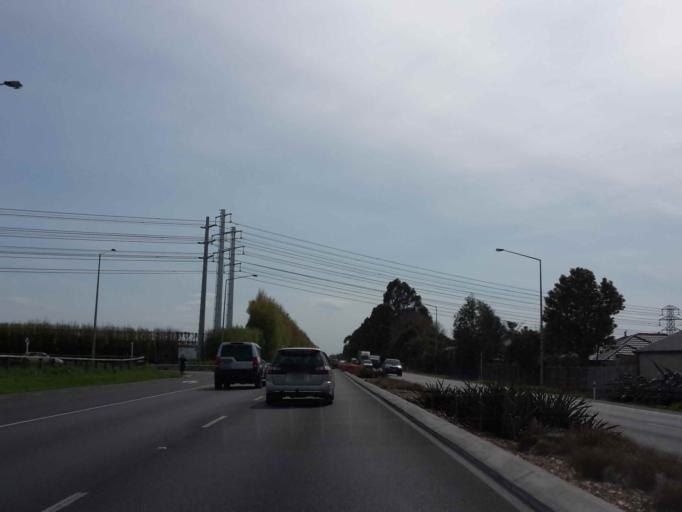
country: NZ
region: Canterbury
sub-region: Selwyn District
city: Prebbleton
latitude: -43.5132
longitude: 172.5382
